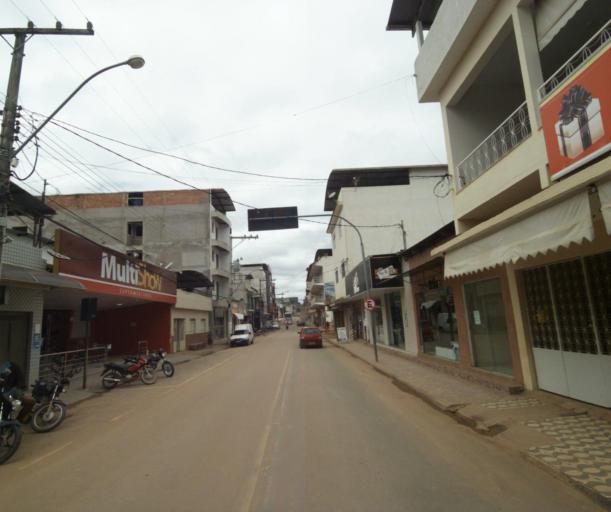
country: BR
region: Espirito Santo
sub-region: Irupi
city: Irupi
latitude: -20.3450
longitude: -41.6405
